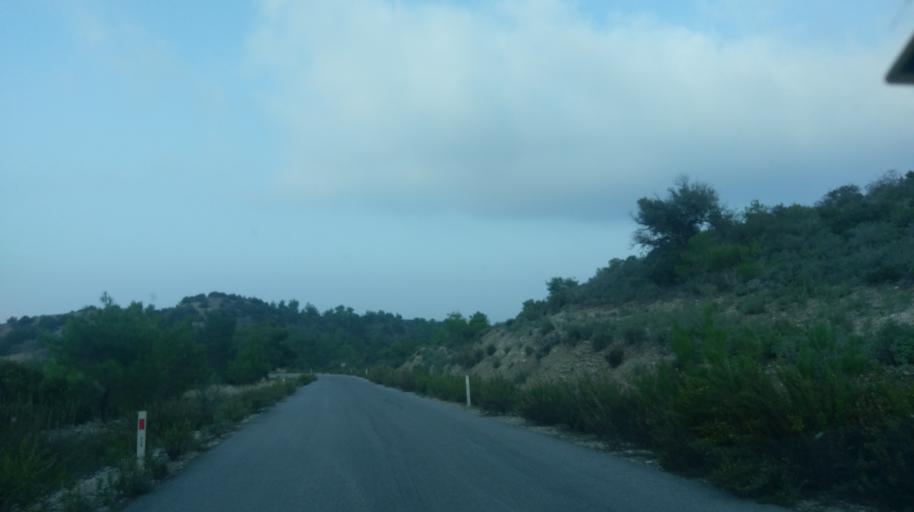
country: CY
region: Ammochostos
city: Trikomo
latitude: 35.3884
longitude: 33.8594
